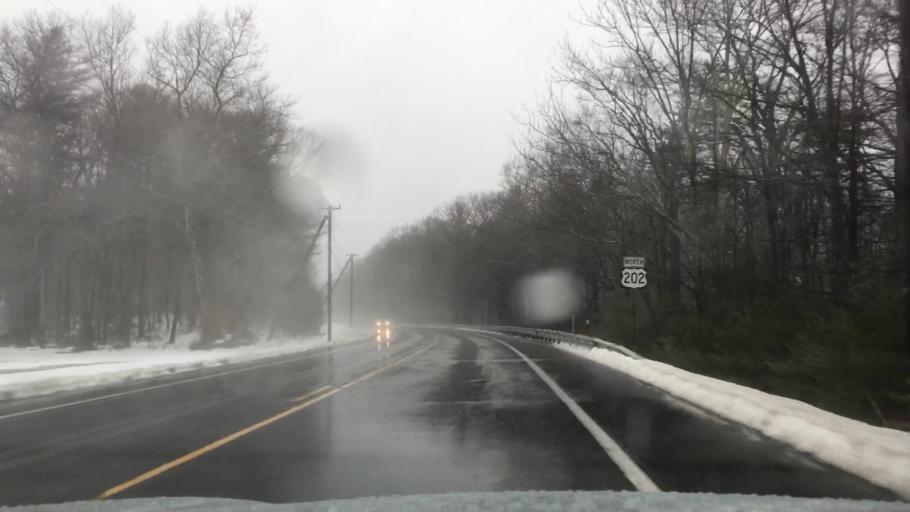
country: US
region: Massachusetts
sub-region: Hampshire County
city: Pelham
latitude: 42.3654
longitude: -72.3985
